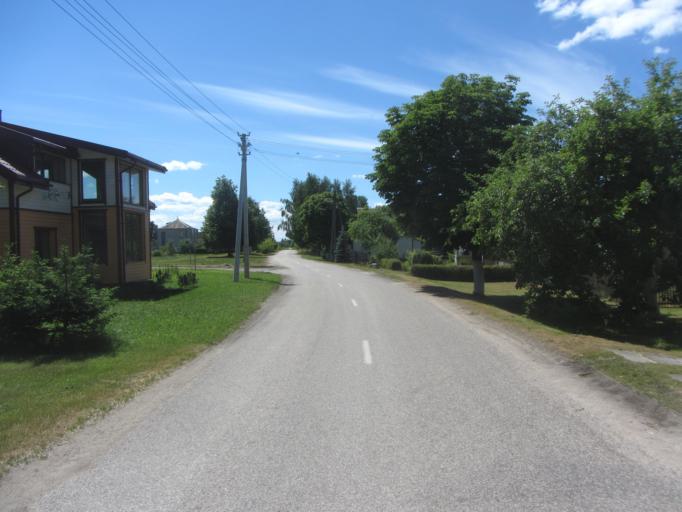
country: LT
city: Birstonas
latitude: 54.7320
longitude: 24.1120
